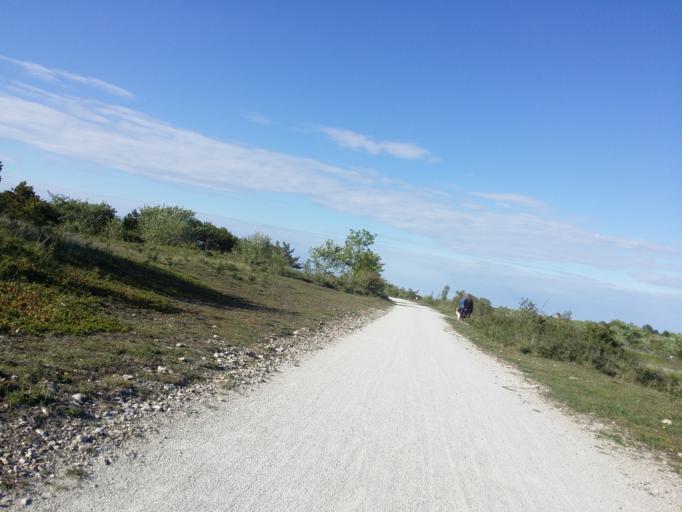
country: SE
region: Gotland
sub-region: Gotland
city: Vibble
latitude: 57.6193
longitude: 18.2651
